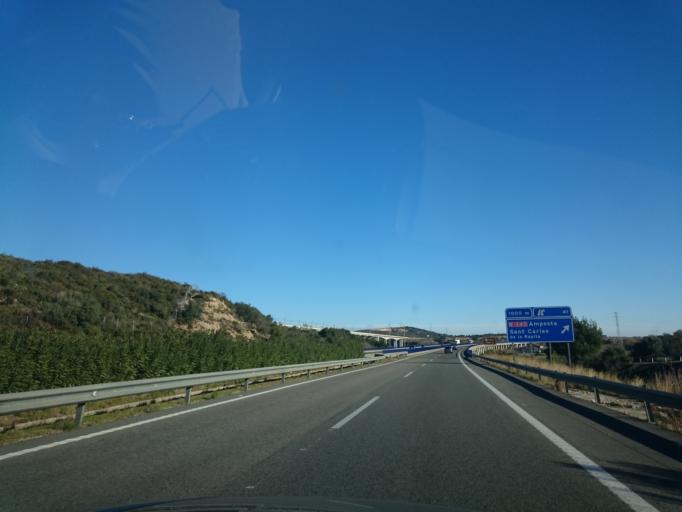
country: ES
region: Catalonia
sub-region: Provincia de Tarragona
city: Amposta
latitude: 40.7235
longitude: 0.5664
